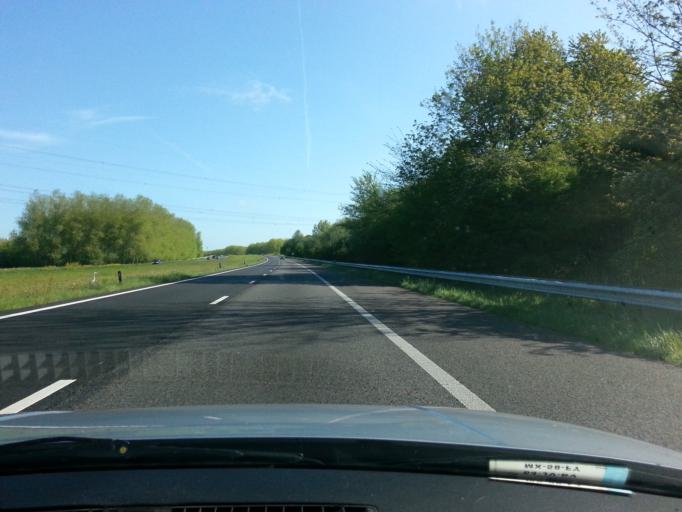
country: NL
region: Flevoland
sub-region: Gemeente Lelystad
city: Lelystad
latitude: 52.4951
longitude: 5.5267
